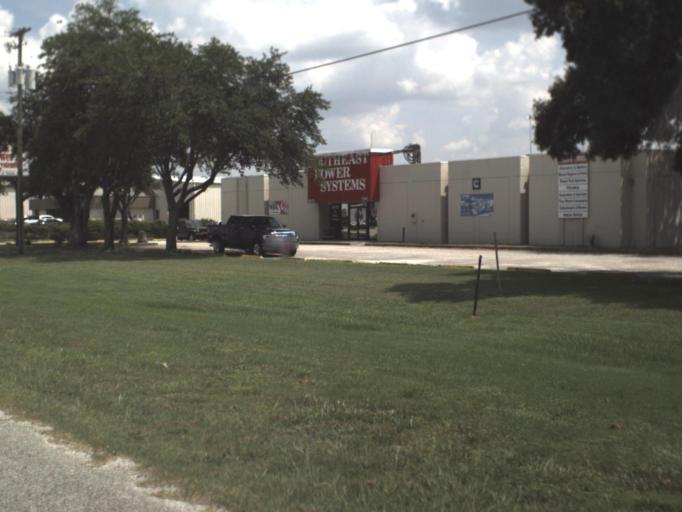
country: US
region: Florida
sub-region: Hillsborough County
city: Palm River-Clair Mel
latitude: 27.9521
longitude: -82.3821
